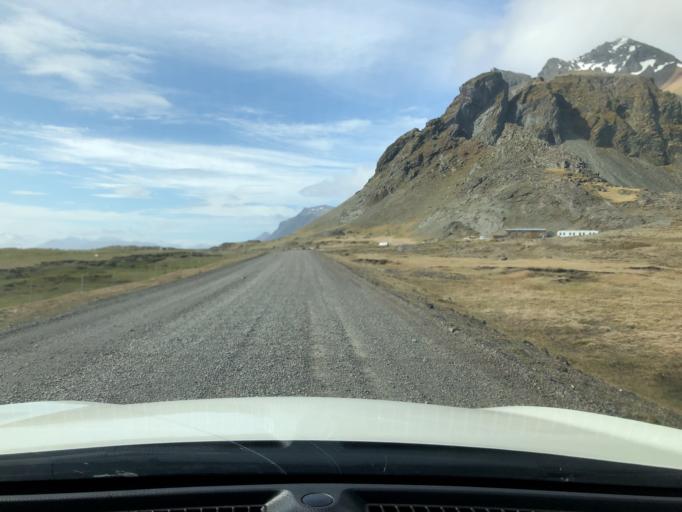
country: IS
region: East
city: Hoefn
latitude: 64.2532
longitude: -14.9917
